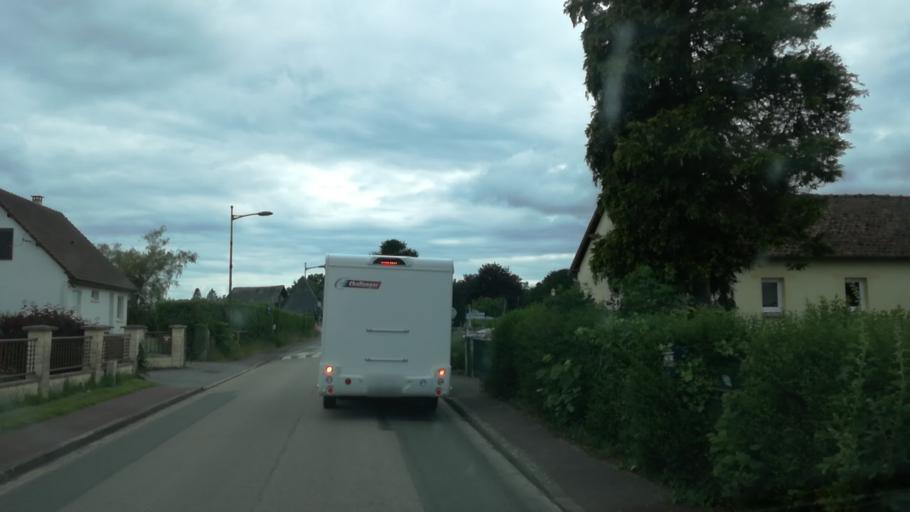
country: FR
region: Haute-Normandie
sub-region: Departement de l'Eure
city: Bourg-Achard
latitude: 49.3234
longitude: 0.8088
